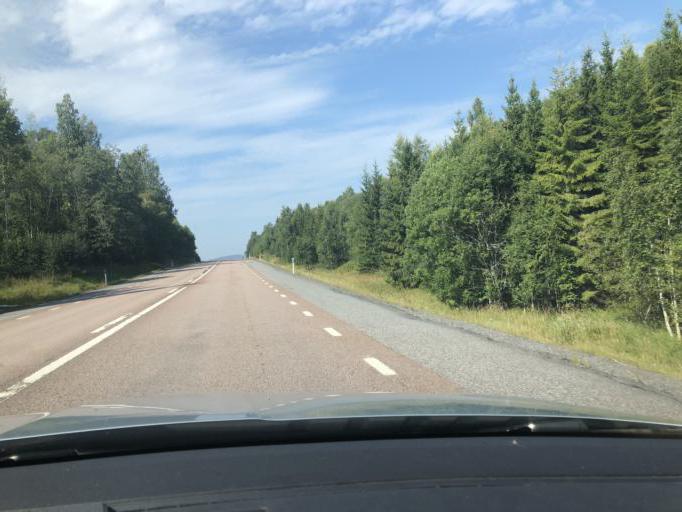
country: SE
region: Vaesternorrland
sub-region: Haernoesands Kommun
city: Haernoesand
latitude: 62.7939
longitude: 17.8964
